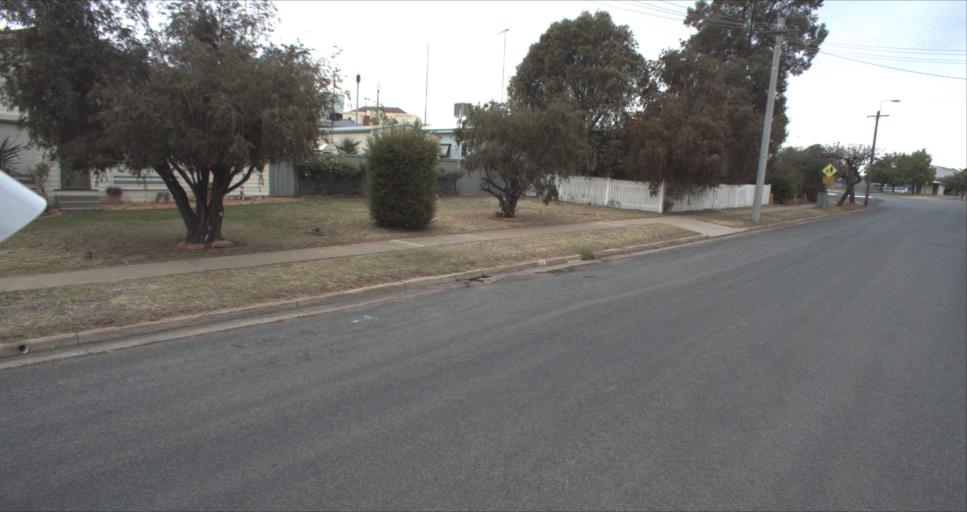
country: AU
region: New South Wales
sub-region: Leeton
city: Leeton
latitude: -34.5496
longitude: 146.4049
